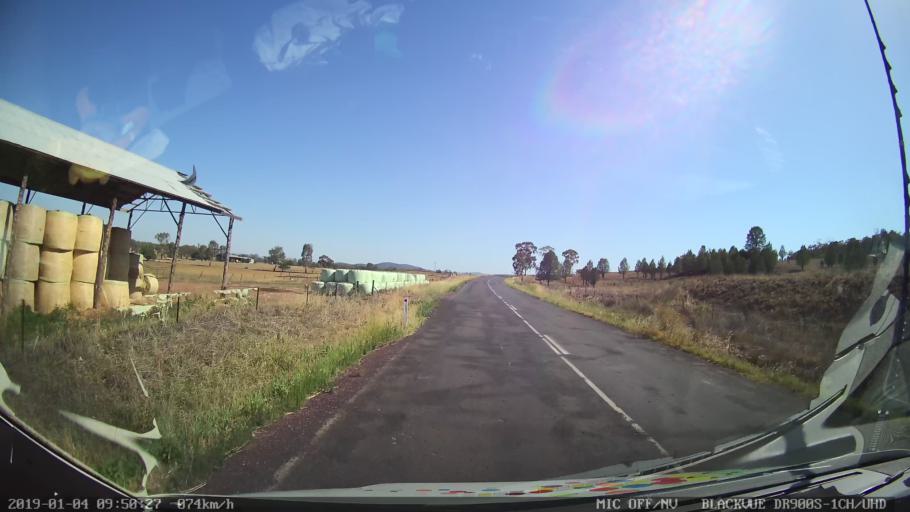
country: AU
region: New South Wales
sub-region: Cabonne
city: Canowindra
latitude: -33.5841
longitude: 148.4154
